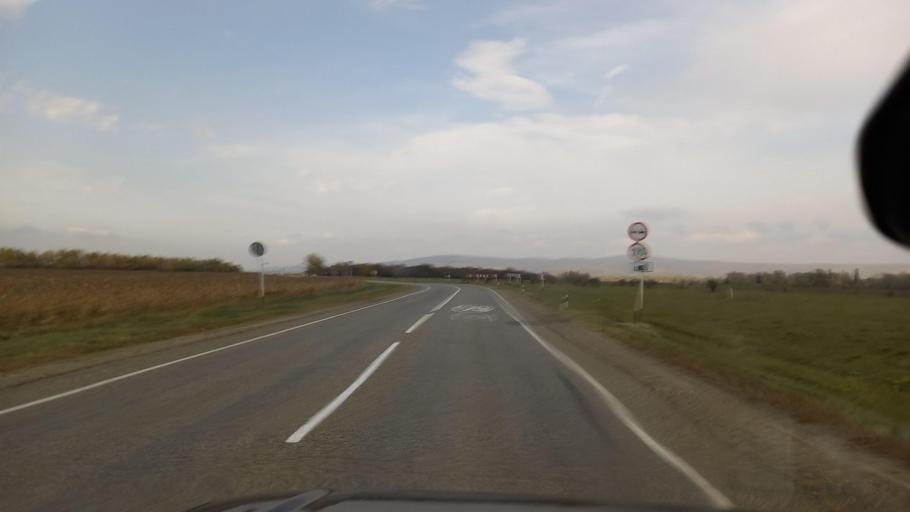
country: RU
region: Krasnodarskiy
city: Shedok
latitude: 44.2682
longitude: 40.8699
